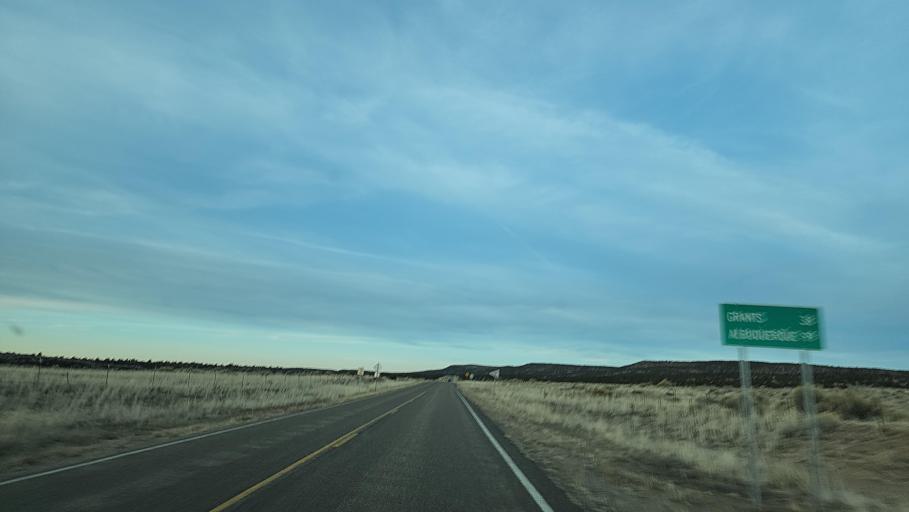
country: US
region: New Mexico
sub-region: Cibola County
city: Grants
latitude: 34.7123
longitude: -107.9879
